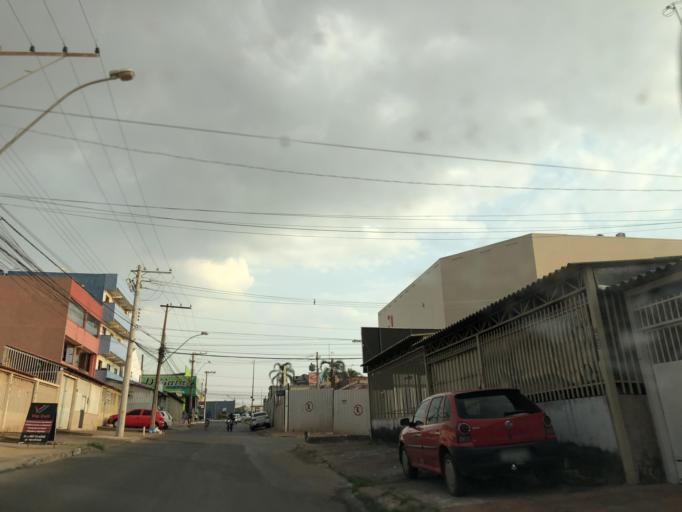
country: BR
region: Federal District
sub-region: Brasilia
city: Brasilia
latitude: -15.9021
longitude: -48.0638
